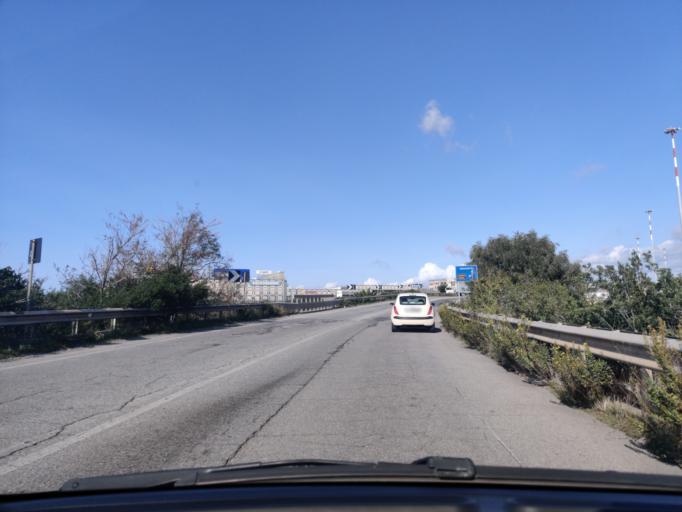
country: IT
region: Latium
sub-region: Citta metropolitana di Roma Capitale
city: Aurelia
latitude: 42.1220
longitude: 11.7704
